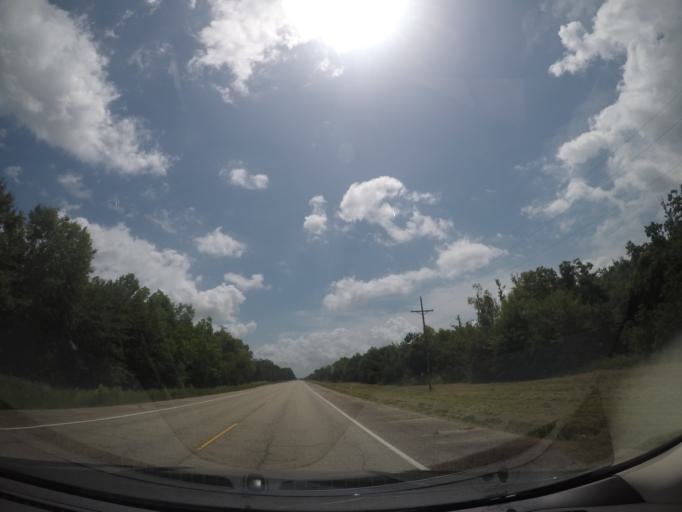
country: US
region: Mississippi
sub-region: Hancock County
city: Pearlington
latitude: 30.2322
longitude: -89.6615
